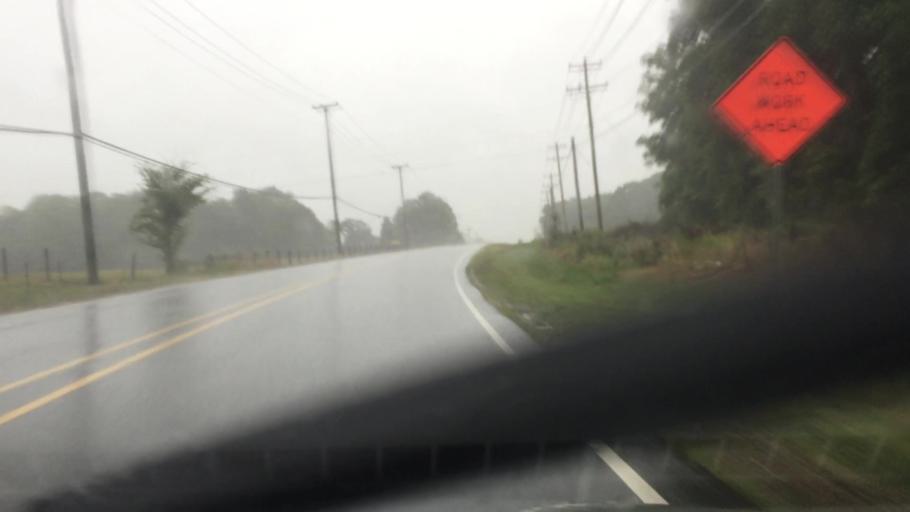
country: US
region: North Carolina
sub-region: Cabarrus County
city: Kannapolis
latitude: 35.4373
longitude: -80.6927
